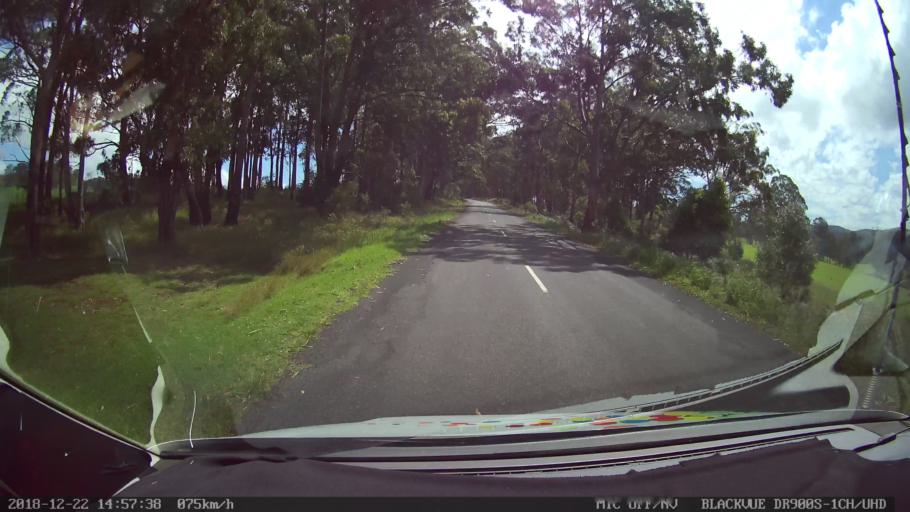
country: AU
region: New South Wales
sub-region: Bellingen
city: Dorrigo
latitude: -30.2355
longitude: 152.4990
